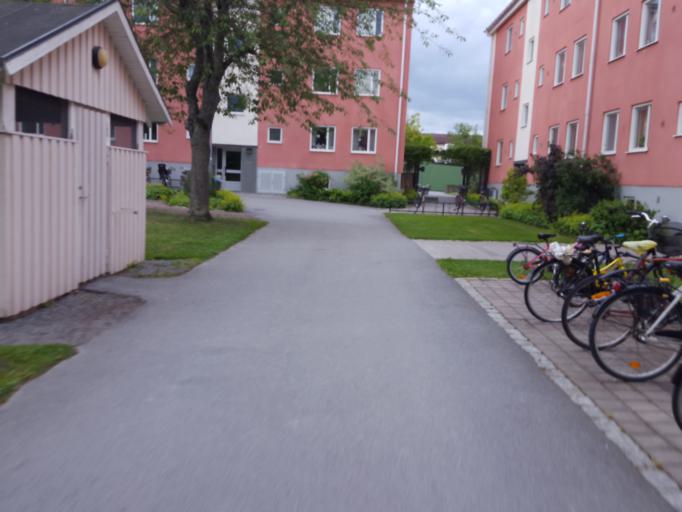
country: SE
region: Uppsala
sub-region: Uppsala Kommun
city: Uppsala
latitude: 59.8723
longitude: 17.6660
